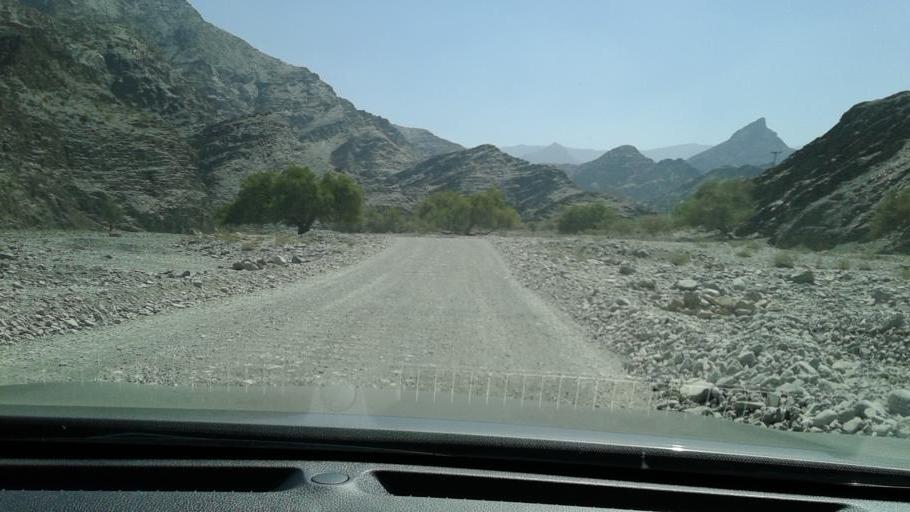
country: OM
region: Al Batinah
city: Bayt al `Awabi
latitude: 23.2666
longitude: 57.4470
